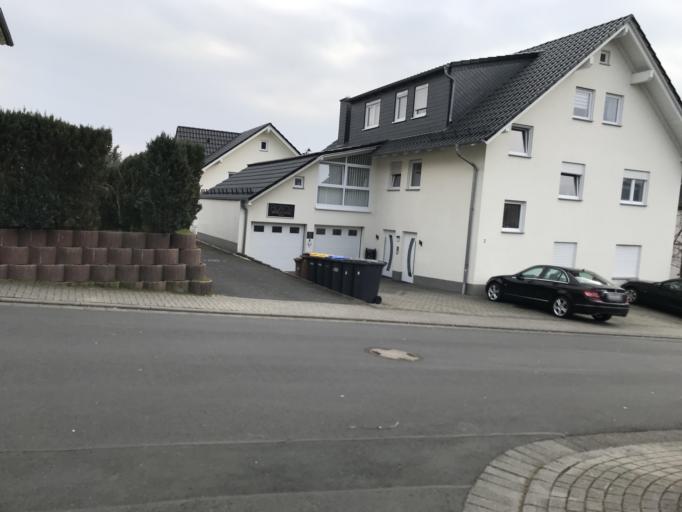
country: DE
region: Hesse
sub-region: Regierungsbezirk Giessen
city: Sinn
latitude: 50.6552
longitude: 8.3304
